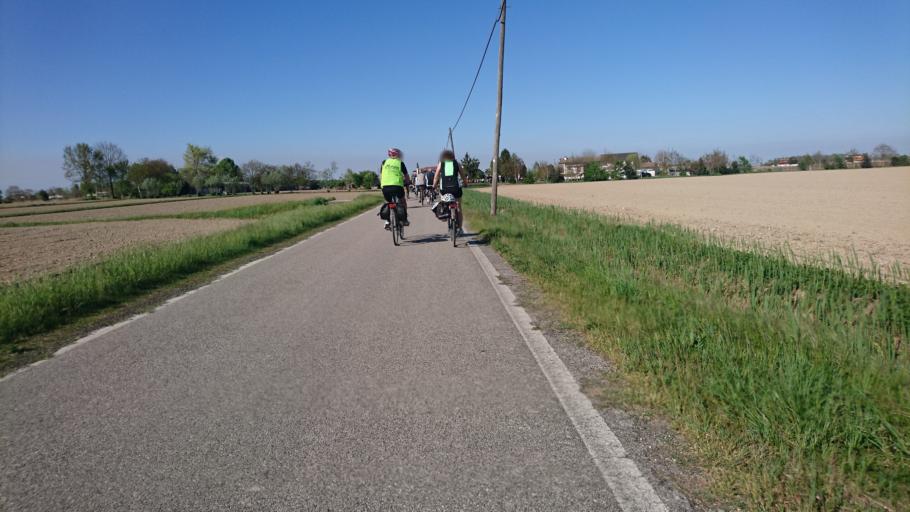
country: IT
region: Veneto
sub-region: Provincia di Venezia
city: Eraclea
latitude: 45.5929
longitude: 12.6644
